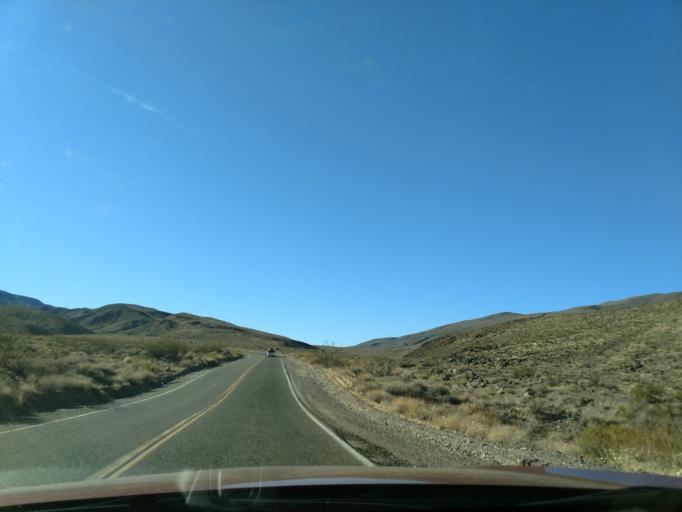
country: US
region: Nevada
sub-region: Nye County
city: Beatty
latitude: 36.4407
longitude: -117.2478
